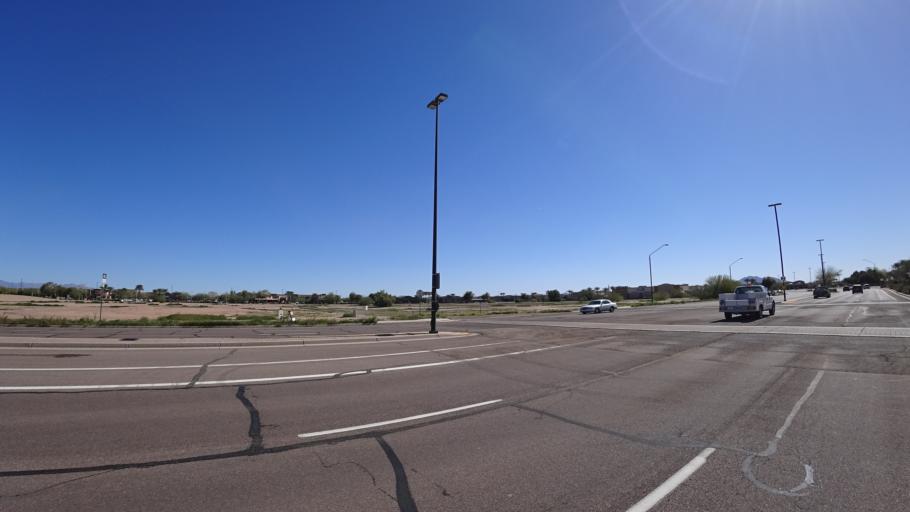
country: US
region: Arizona
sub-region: Maricopa County
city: Gilbert
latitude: 33.3036
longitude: -111.7471
